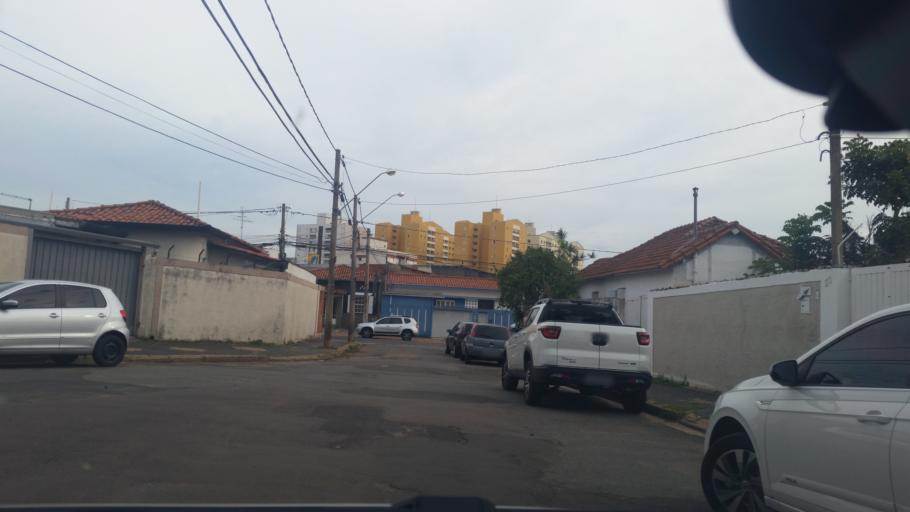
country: BR
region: Sao Paulo
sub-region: Campinas
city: Campinas
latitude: -22.8844
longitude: -47.0617
